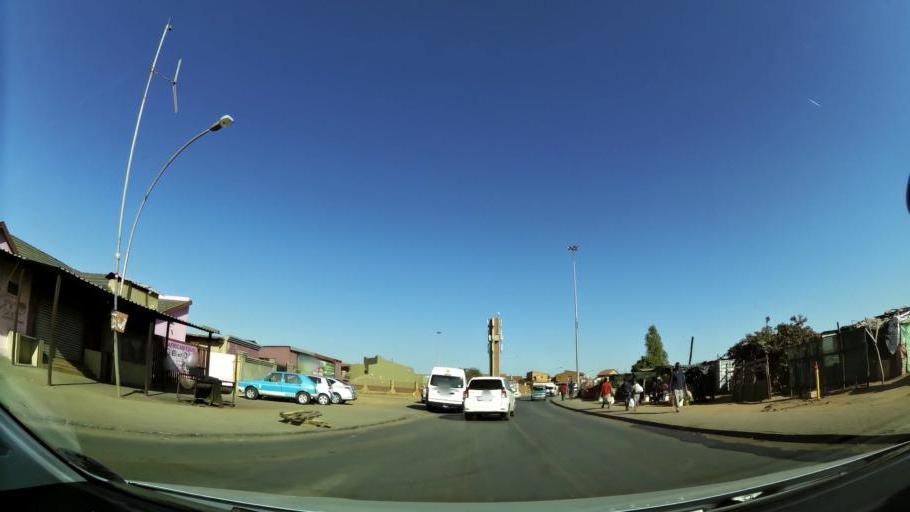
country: ZA
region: Gauteng
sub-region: Ekurhuleni Metropolitan Municipality
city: Tembisa
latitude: -26.0172
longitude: 28.2308
